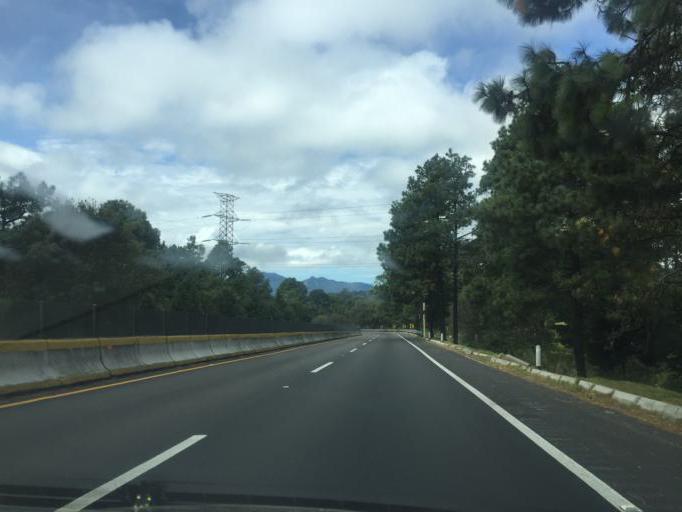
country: MX
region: Morelos
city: Tres Marias
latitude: 19.0840
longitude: -99.2278
